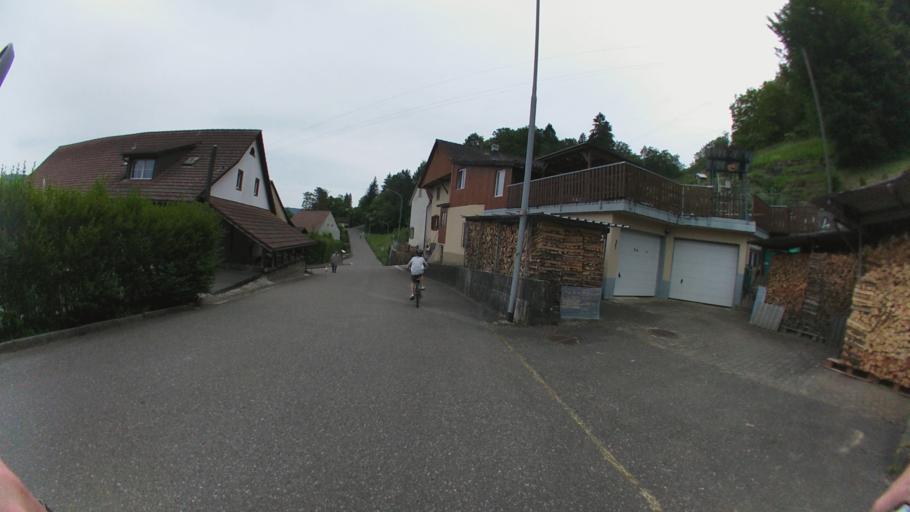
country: CH
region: Aargau
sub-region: Bezirk Zurzach
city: Bad Zurzach
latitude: 47.6006
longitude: 8.2770
